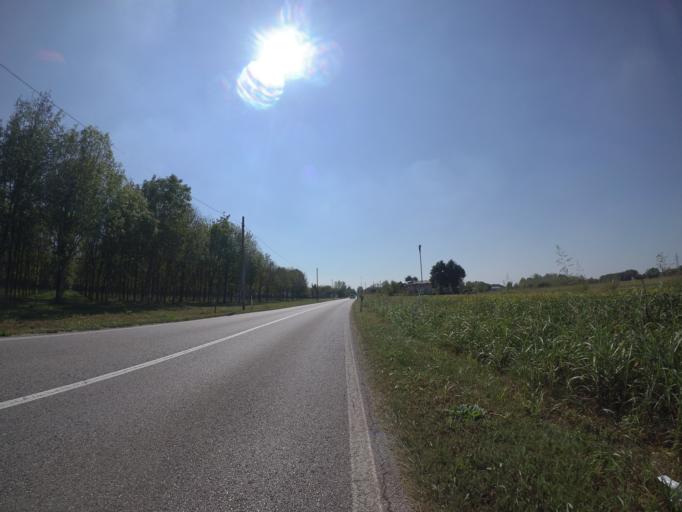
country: IT
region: Friuli Venezia Giulia
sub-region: Provincia di Udine
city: Codroipo
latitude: 45.9797
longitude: 12.9923
